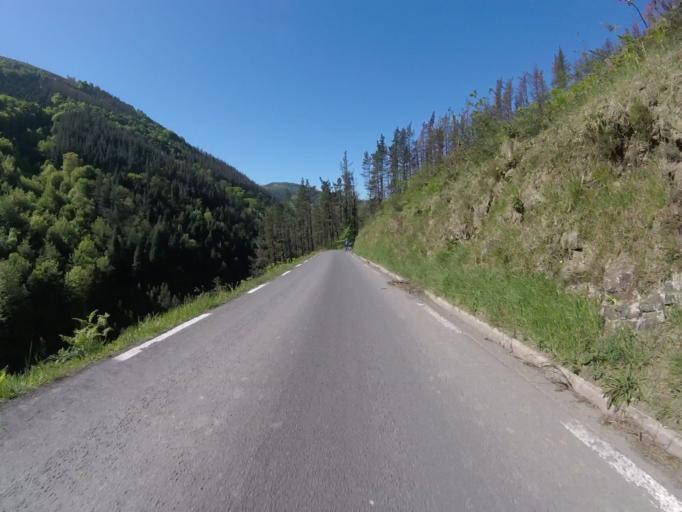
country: ES
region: Basque Country
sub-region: Provincia de Guipuzcoa
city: Errezil
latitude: 43.1859
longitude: -2.1985
